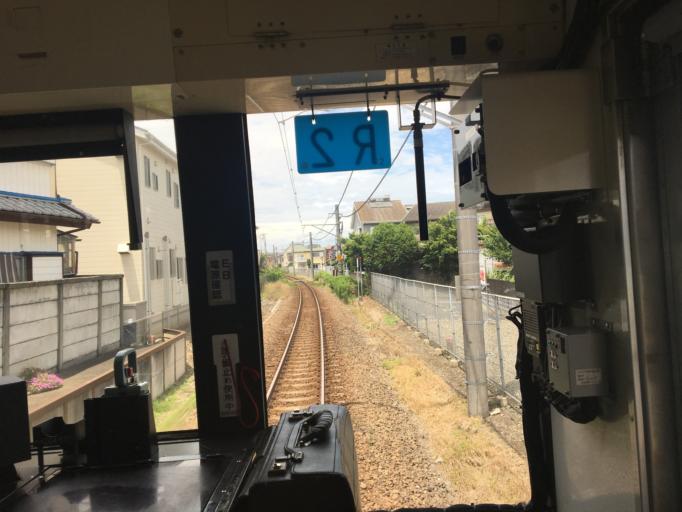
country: JP
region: Kanagawa
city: Chigasaki
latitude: 35.3577
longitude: 139.3995
